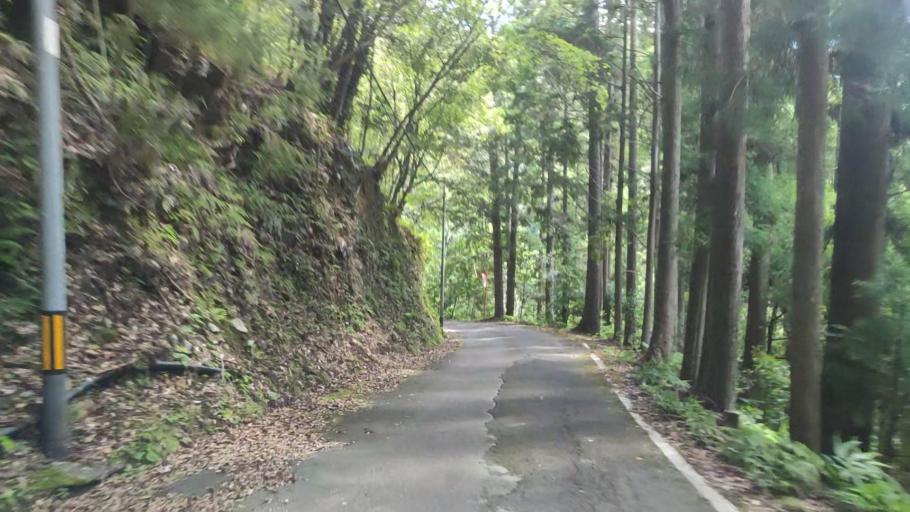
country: JP
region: Wakayama
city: Shingu
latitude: 33.9061
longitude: 135.8688
